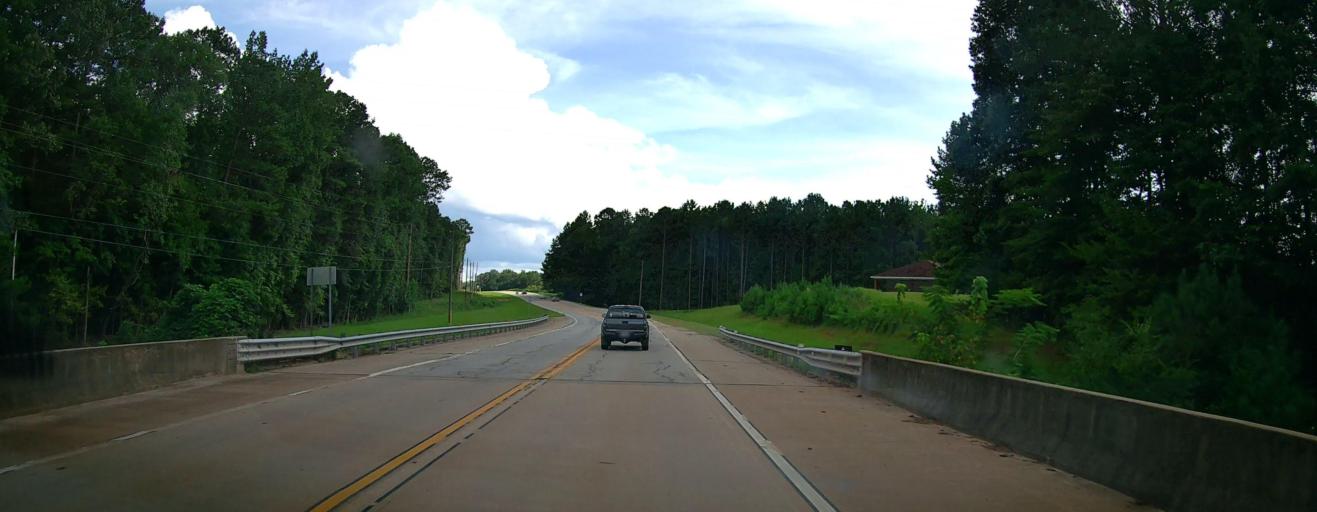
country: US
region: Georgia
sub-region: Harris County
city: Hamilton
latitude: 32.7084
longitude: -84.8699
